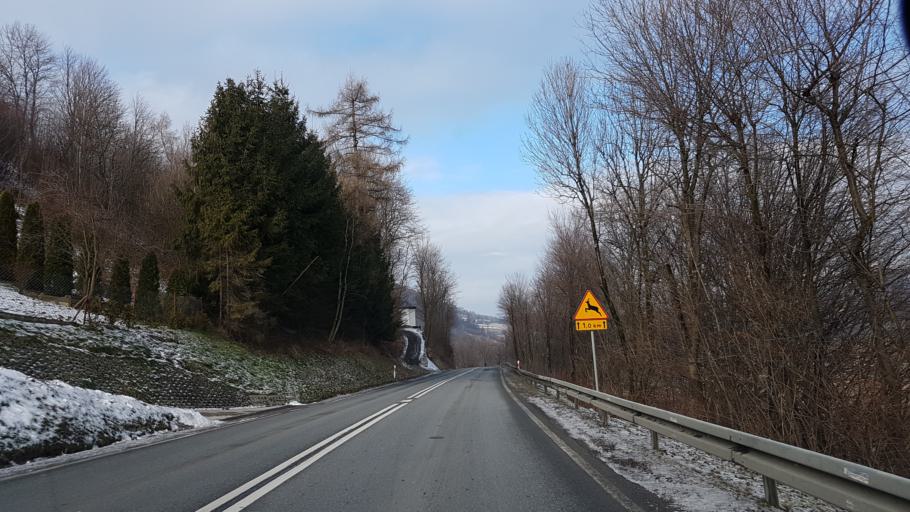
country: PL
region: Lesser Poland Voivodeship
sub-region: Powiat nowosadecki
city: Rytro
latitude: 49.4748
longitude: 20.6839
